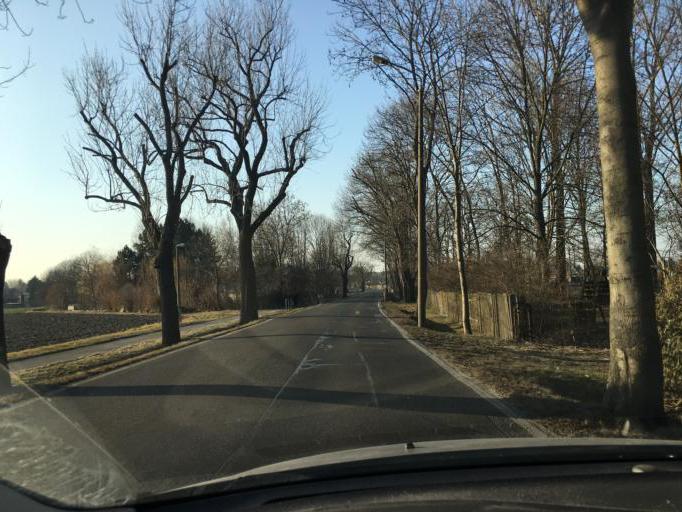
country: DE
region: Saxony
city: Leipzig
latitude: 51.3156
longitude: 12.4377
